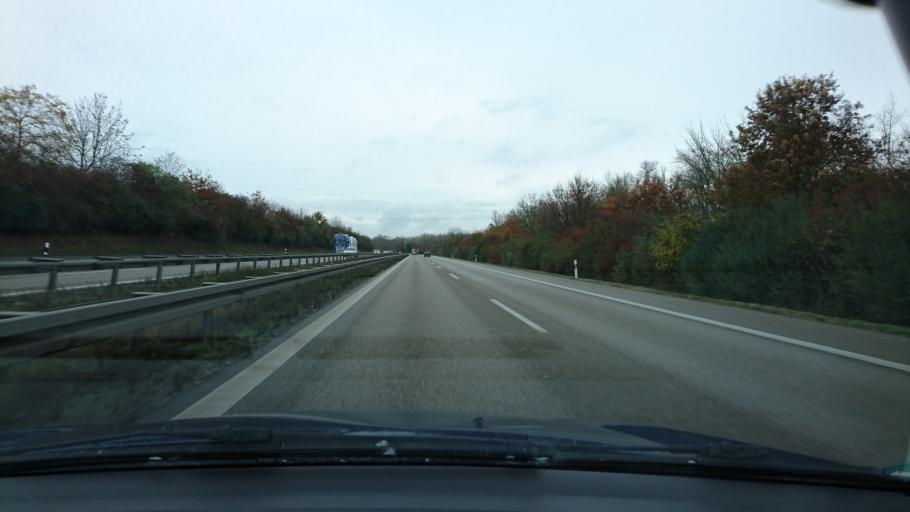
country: DE
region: Bavaria
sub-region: Swabia
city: Langweid
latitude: 48.4678
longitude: 10.8791
